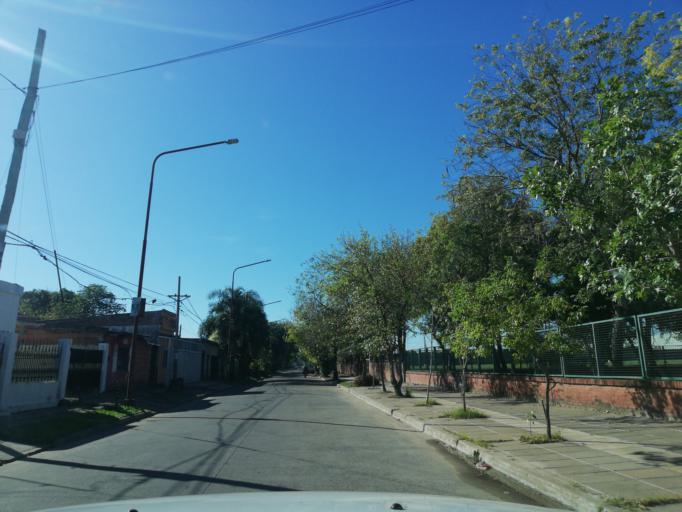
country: AR
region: Corrientes
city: Corrientes
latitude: -27.4752
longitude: -58.8174
